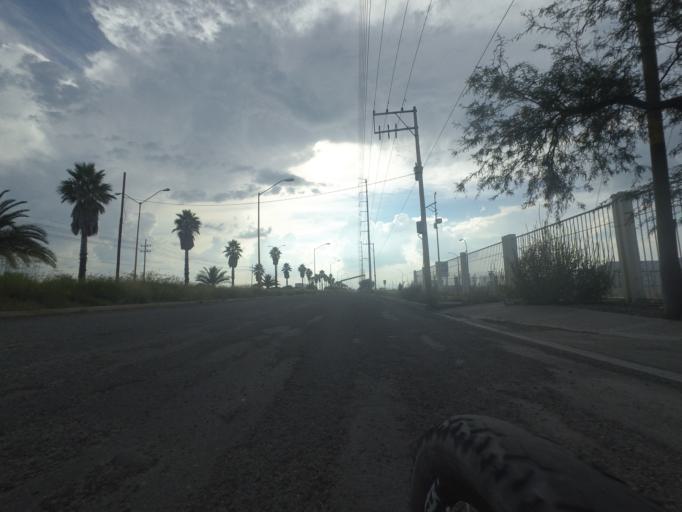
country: MX
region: Aguascalientes
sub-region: Aguascalientes
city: Penuelas (El Cienegal)
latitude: 21.7253
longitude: -102.2967
